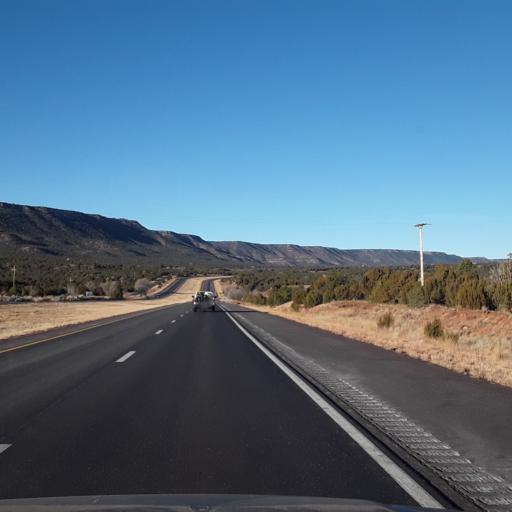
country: US
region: New Mexico
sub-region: San Miguel County
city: Pecos
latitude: 35.4157
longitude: -105.5261
